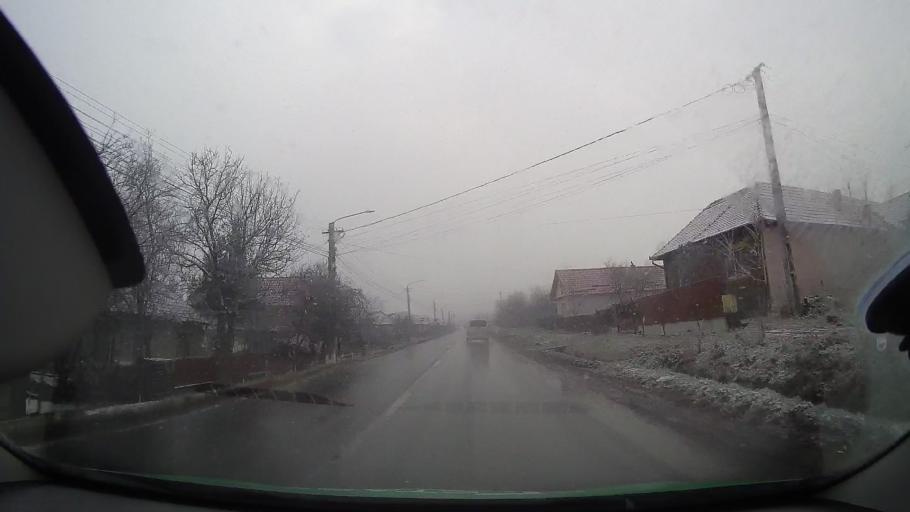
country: RO
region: Mures
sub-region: Comuna Bagaciu
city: Delenii
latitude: 46.2837
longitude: 24.3006
